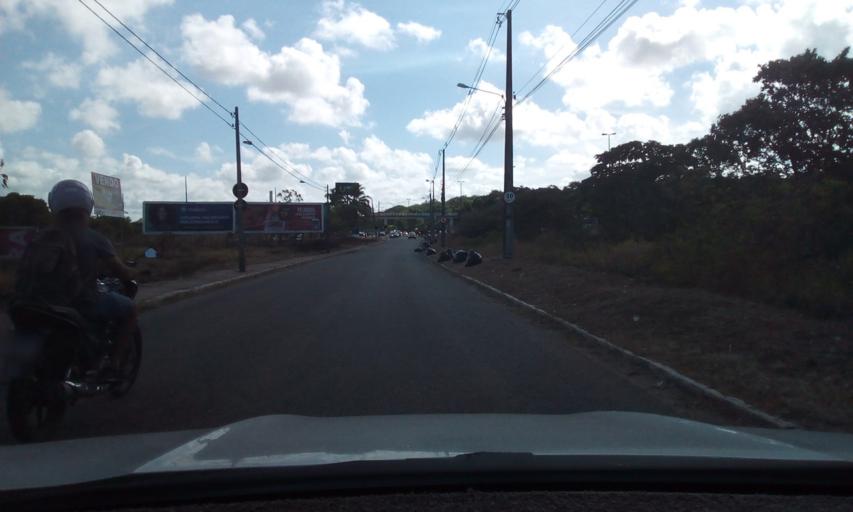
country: BR
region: Paraiba
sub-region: Joao Pessoa
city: Joao Pessoa
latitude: -7.1560
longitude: -34.8567
